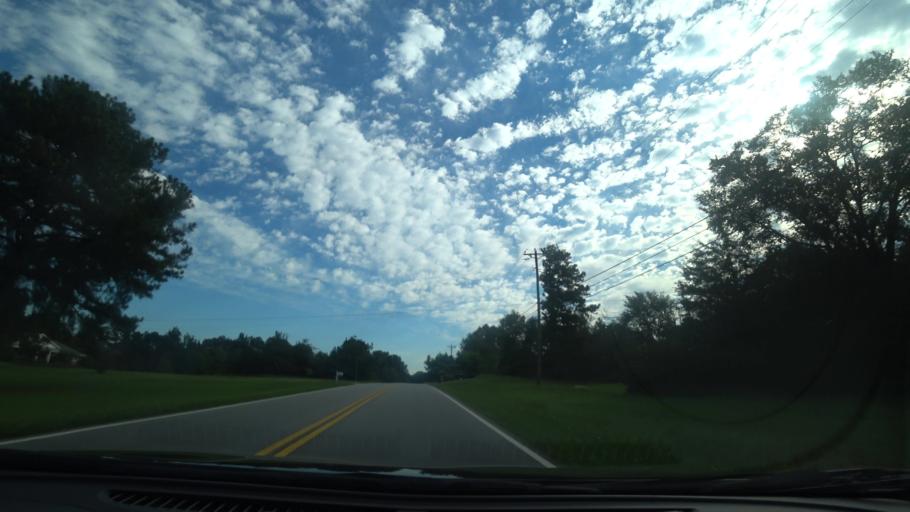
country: US
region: Georgia
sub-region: Rockdale County
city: Lakeview Estates
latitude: 33.7306
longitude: -83.9963
